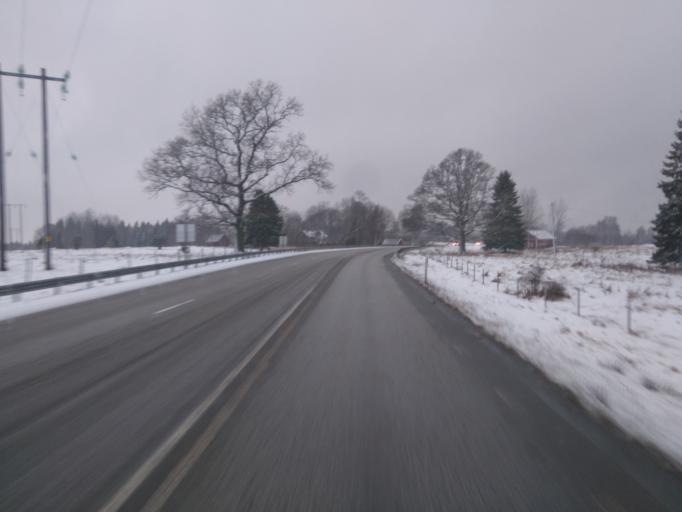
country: SE
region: Joenkoeping
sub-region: Eksjo Kommun
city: Eksjoe
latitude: 57.6393
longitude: 15.0867
